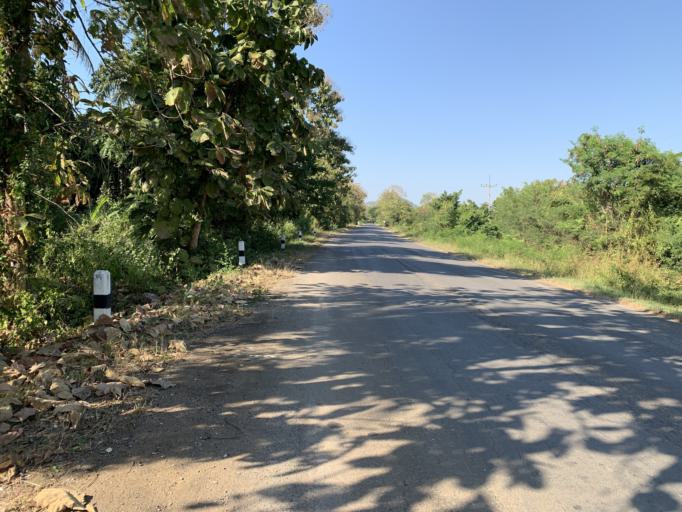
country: TH
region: Sukhothai
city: Thung Saliam
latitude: 17.3569
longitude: 99.5438
